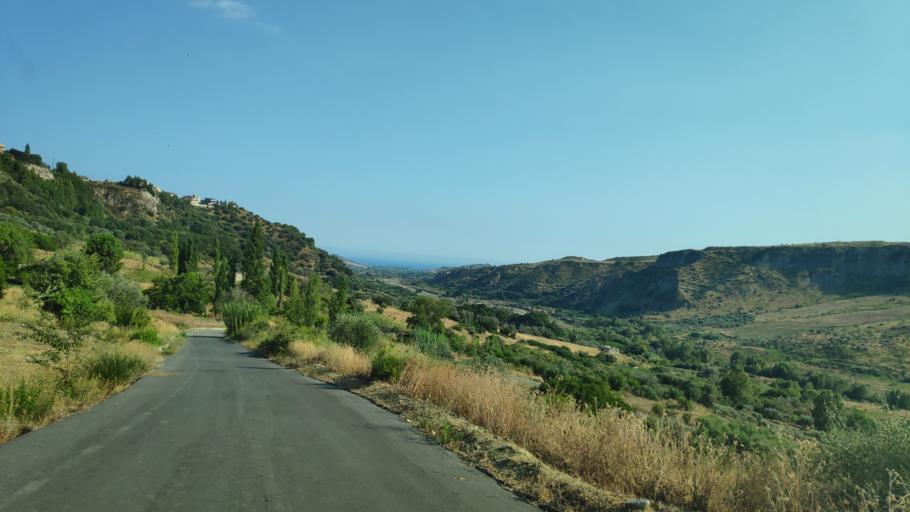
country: IT
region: Calabria
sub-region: Provincia di Reggio Calabria
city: Placanica
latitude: 38.4146
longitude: 16.4450
